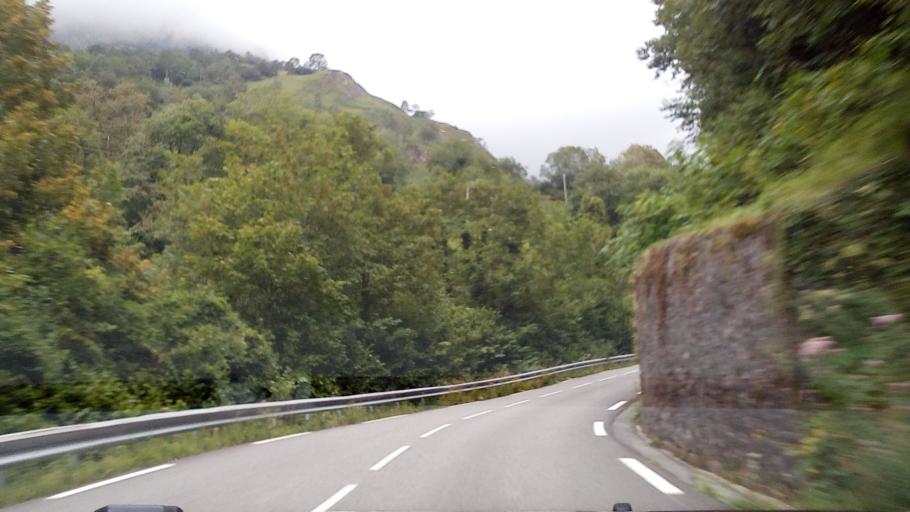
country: FR
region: Aquitaine
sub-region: Departement des Pyrenees-Atlantiques
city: Laruns
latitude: 42.9719
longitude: -0.3853
